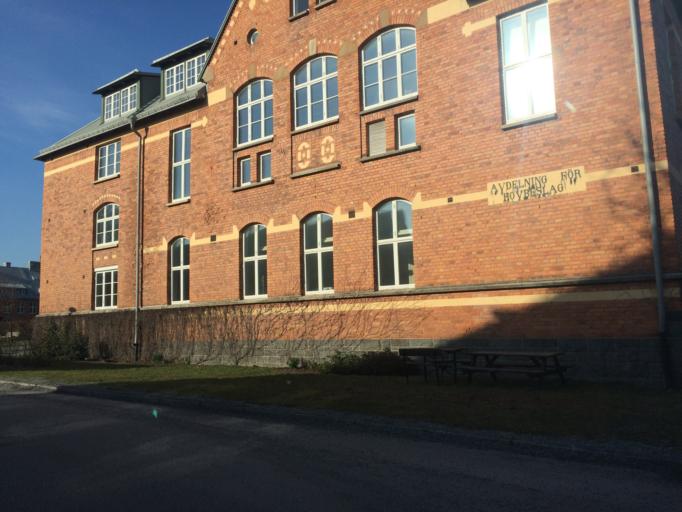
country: SE
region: Stockholm
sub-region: Stockholms Kommun
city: Stockholm
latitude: 59.3573
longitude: 18.0559
